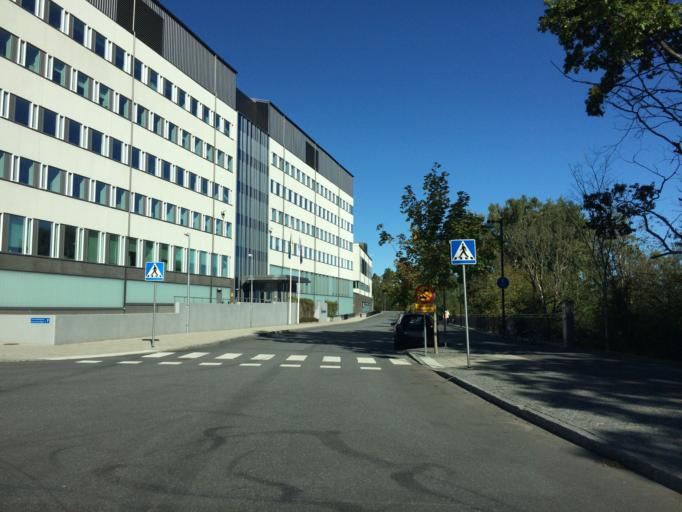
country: SE
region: Stockholm
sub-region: Solna Kommun
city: Solna
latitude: 59.3516
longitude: 18.0112
